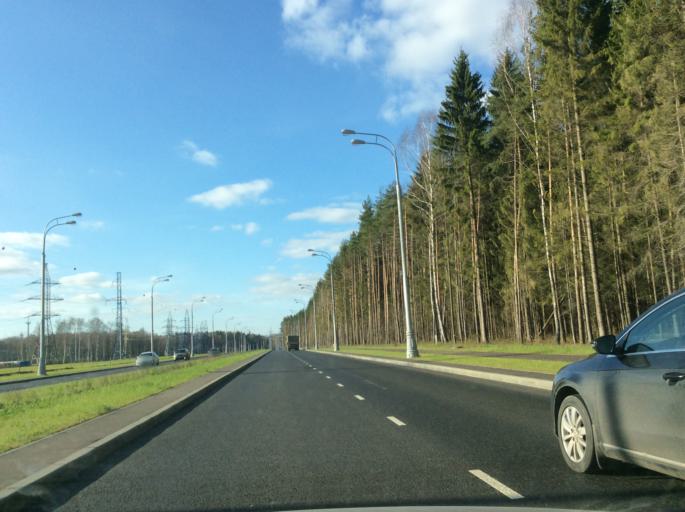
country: RU
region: Moskovskaya
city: Vatutinki
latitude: 55.4836
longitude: 37.3484
